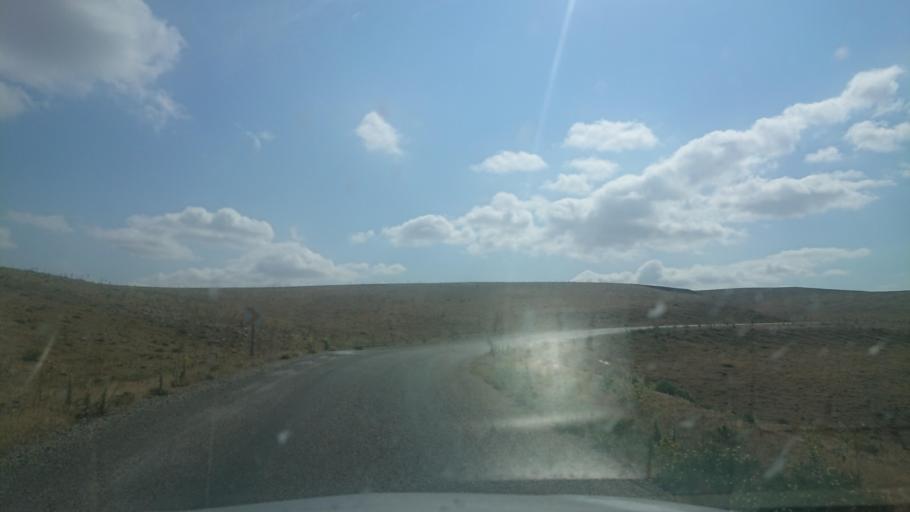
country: TR
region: Aksaray
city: Sariyahsi
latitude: 39.0069
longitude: 33.9557
